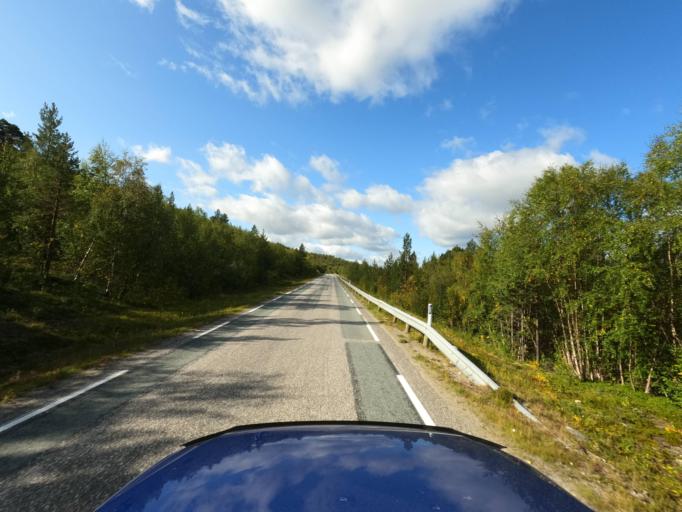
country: NO
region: Finnmark Fylke
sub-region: Karasjok
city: Karasjohka
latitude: 69.4359
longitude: 25.6849
